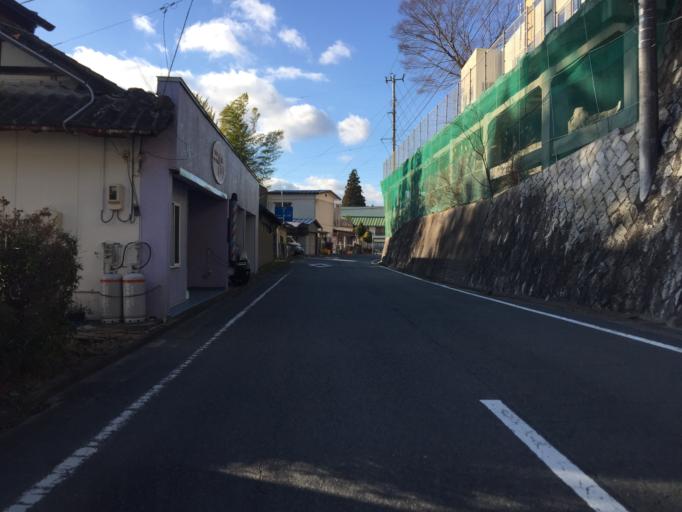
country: JP
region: Fukushima
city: Iwaki
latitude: 37.2069
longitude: 140.7514
